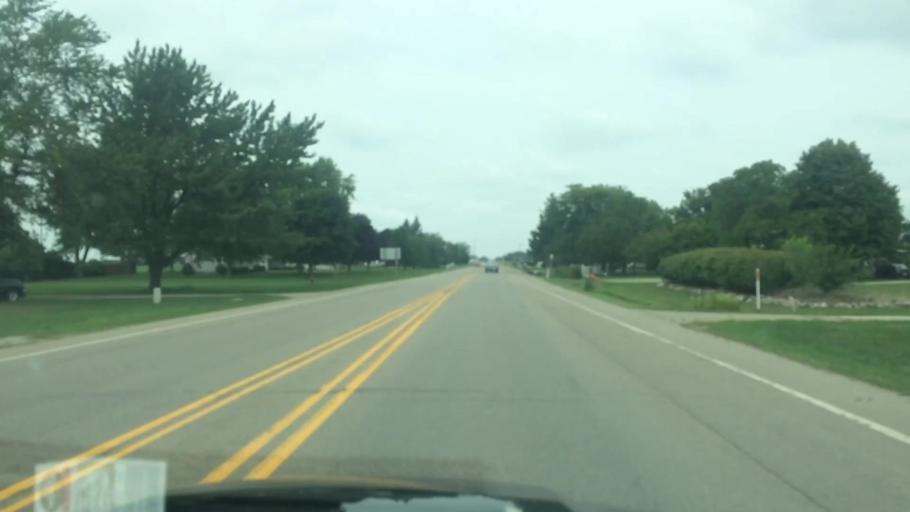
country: US
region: Michigan
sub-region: Huron County
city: Bad Axe
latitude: 43.8275
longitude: -83.0011
